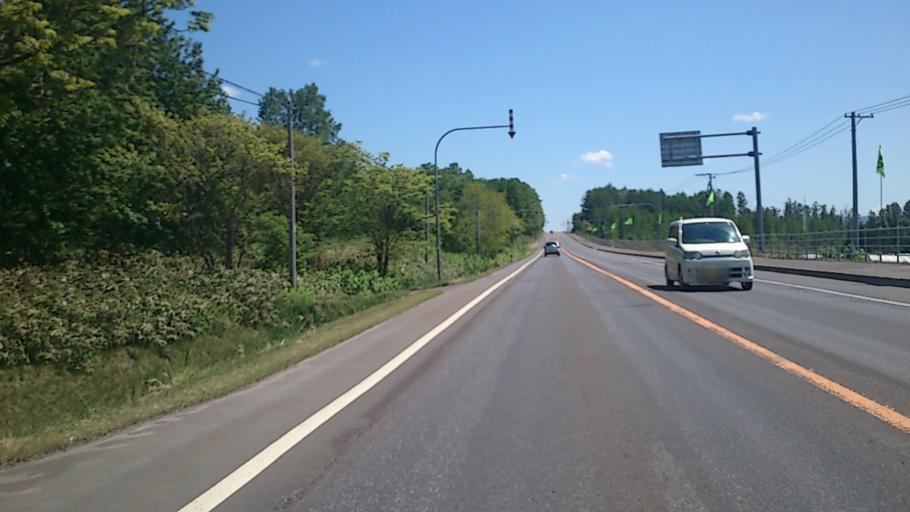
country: JP
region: Hokkaido
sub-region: Asahikawa-shi
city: Asahikawa
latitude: 44.0595
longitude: 142.4031
